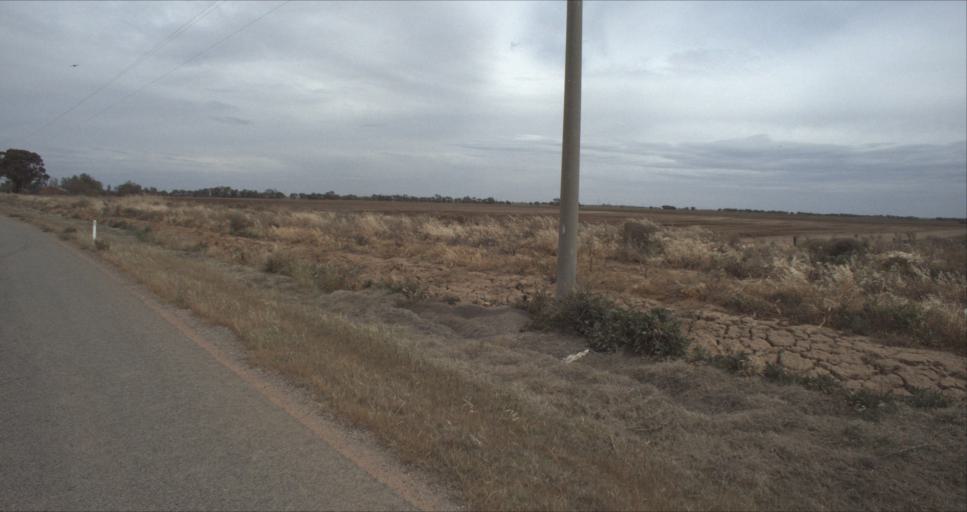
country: AU
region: New South Wales
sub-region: Leeton
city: Leeton
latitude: -34.4345
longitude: 146.3764
